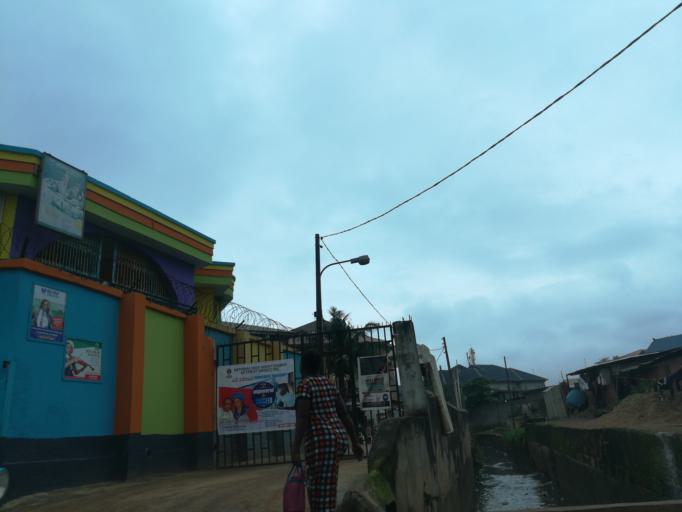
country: NG
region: Lagos
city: Oshodi
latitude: 6.5668
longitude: 3.3407
